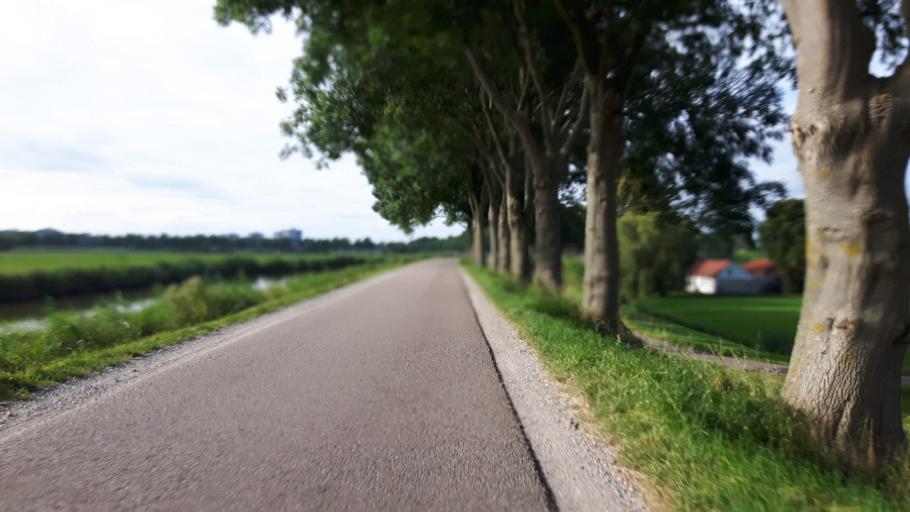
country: NL
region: North Holland
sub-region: Gemeente Purmerend
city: Purmerend
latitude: 52.5385
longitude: 4.9647
